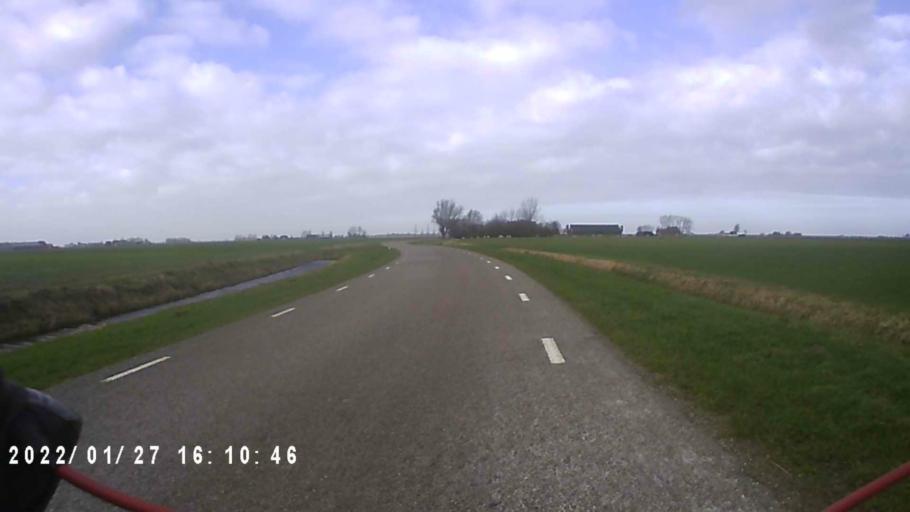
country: NL
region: Friesland
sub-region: Gemeente Dongeradeel
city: Anjum
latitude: 53.3824
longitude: 6.0795
